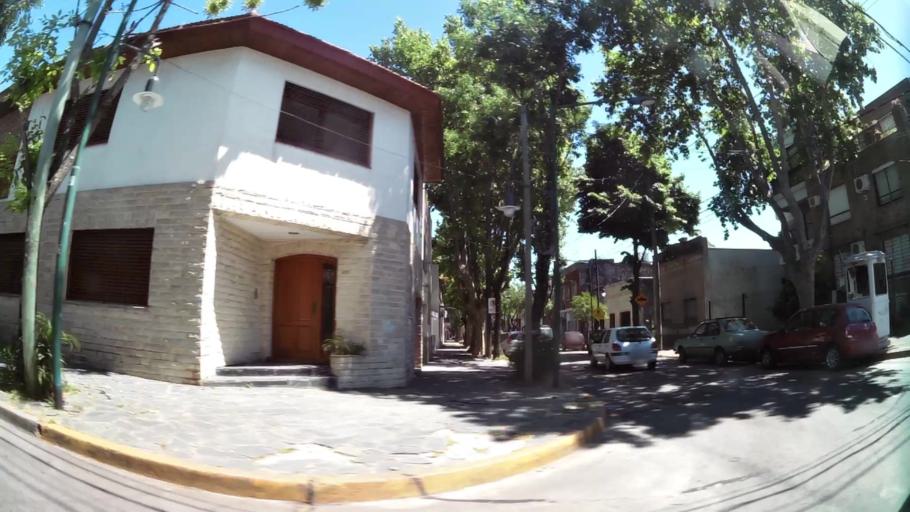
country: AR
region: Buenos Aires
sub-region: Partido de San Isidro
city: San Isidro
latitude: -34.4703
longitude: -58.5233
